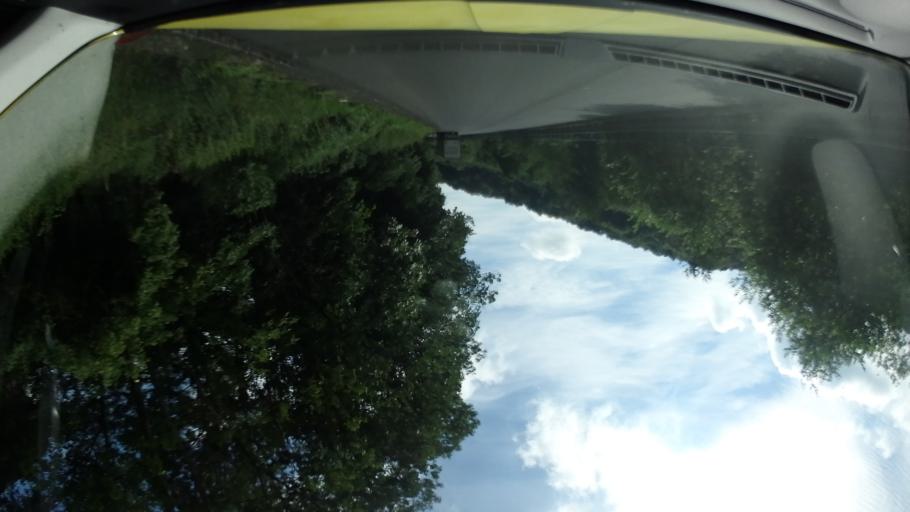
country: CZ
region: Moravskoslezsky
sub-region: Okres Novy Jicin
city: Novy Jicin
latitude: 49.5705
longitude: 18.0243
